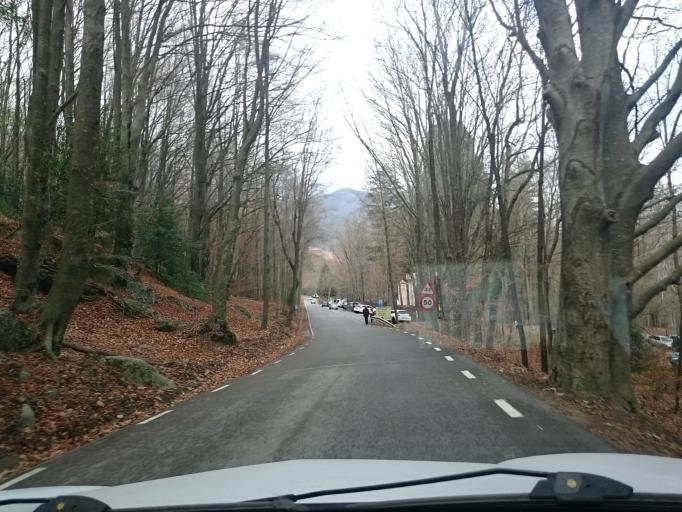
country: ES
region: Catalonia
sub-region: Provincia de Barcelona
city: Fogars de Montclus
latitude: 41.7727
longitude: 2.4641
